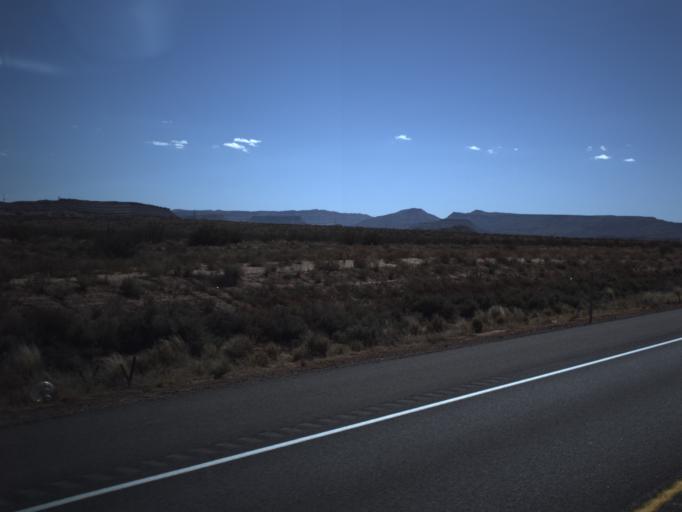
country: US
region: Utah
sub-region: Washington County
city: Washington
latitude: 37.0374
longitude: -113.4852
